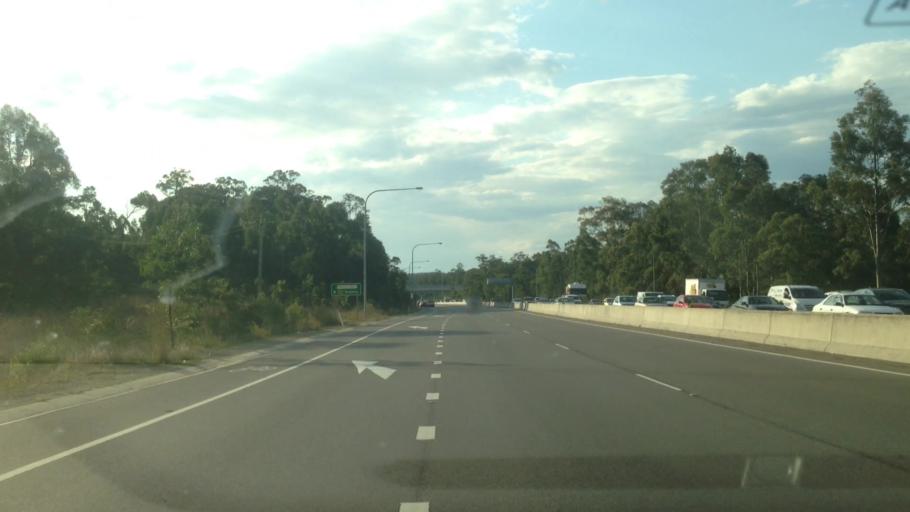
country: AU
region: New South Wales
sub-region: Lake Macquarie Shire
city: Holmesville
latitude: -32.8938
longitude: 151.6062
